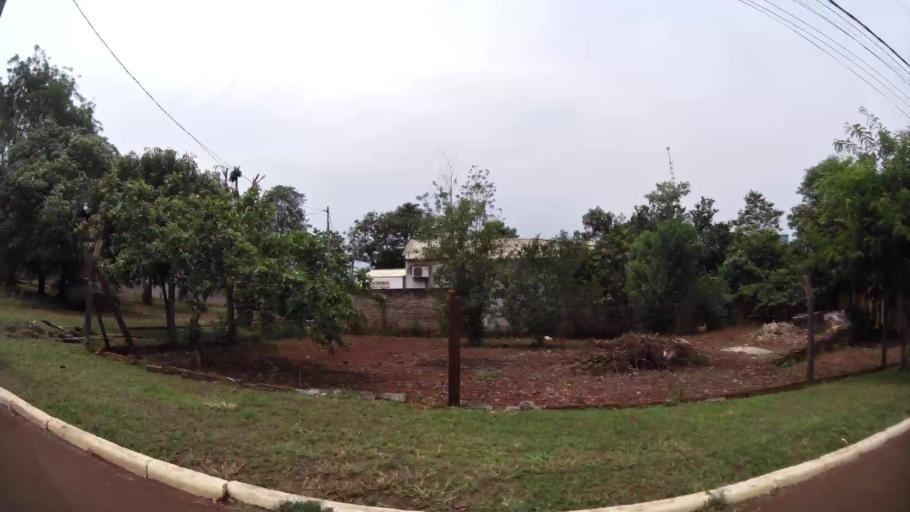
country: PY
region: Alto Parana
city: Presidente Franco
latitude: -25.5572
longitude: -54.6283
